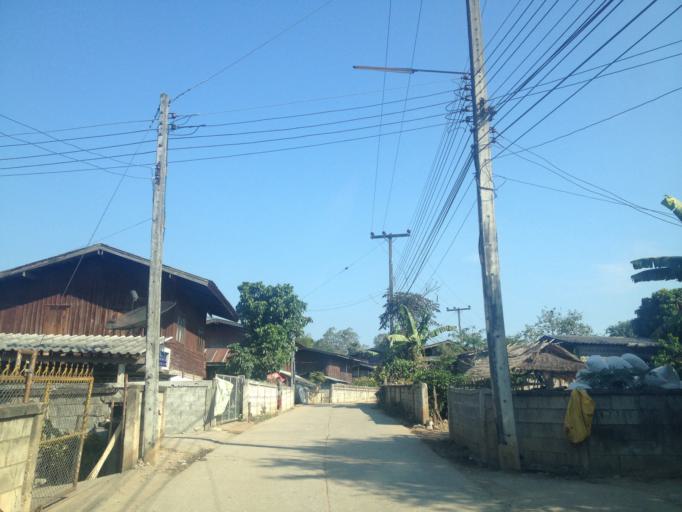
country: TH
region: Mae Hong Son
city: Ban Huai I Huak
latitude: 18.0951
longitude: 98.2055
